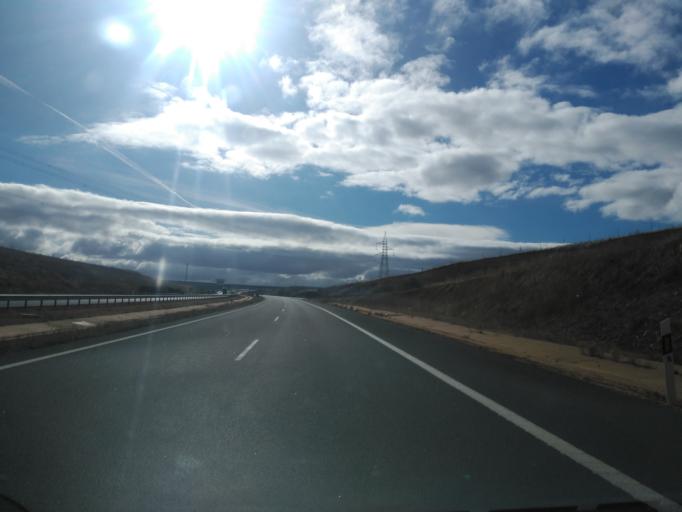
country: ES
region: Castille and Leon
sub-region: Provincia de Palencia
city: Marcilla de Campos
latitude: 42.3622
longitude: -4.3906
